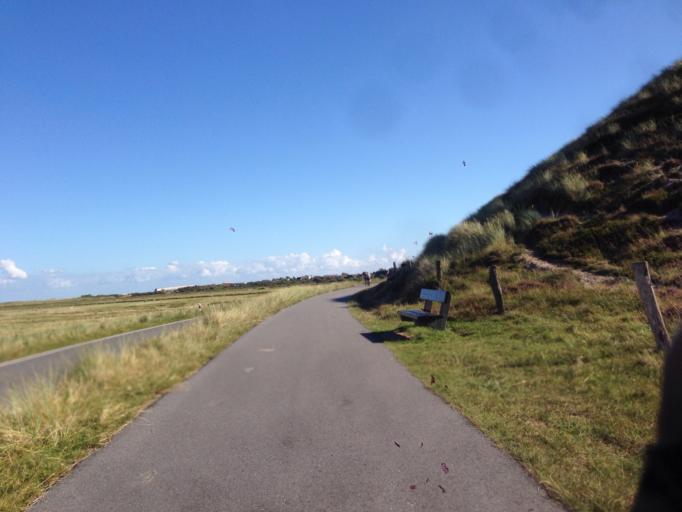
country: DE
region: Schleswig-Holstein
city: List
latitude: 55.0290
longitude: 8.4172
